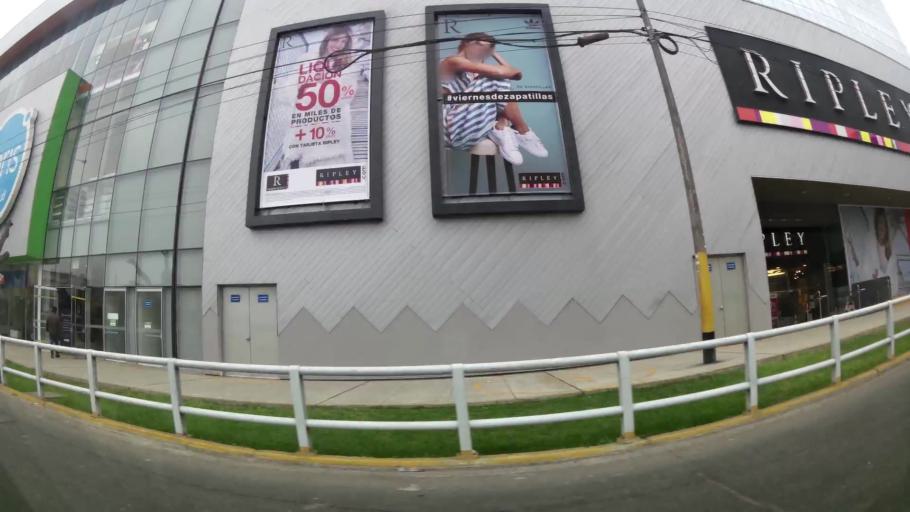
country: PE
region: Lima
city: Lima
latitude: -12.0665
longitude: -77.0468
